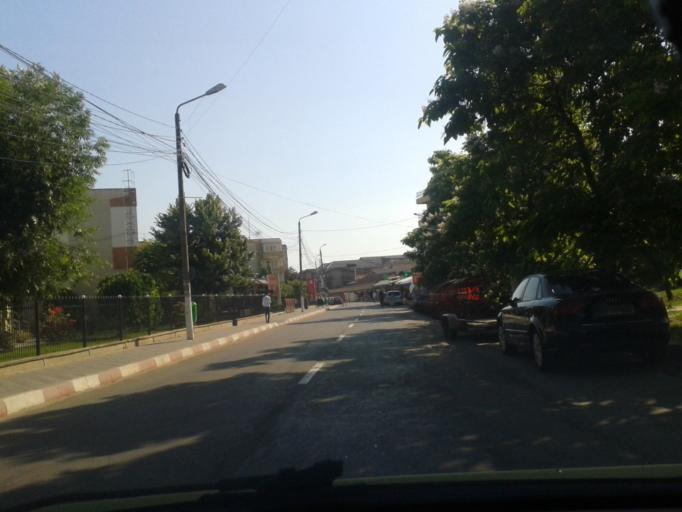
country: RO
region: Constanta
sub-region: Comuna Costinesti
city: Costinesti
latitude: 43.9480
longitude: 28.6329
